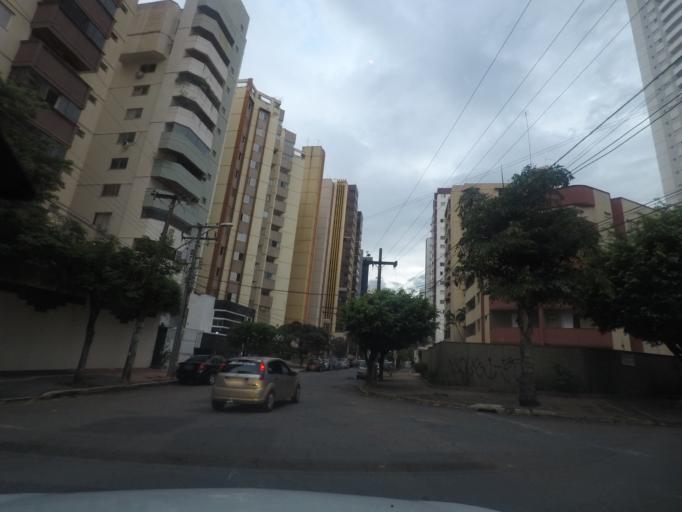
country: BR
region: Goias
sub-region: Goiania
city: Goiania
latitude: -16.7126
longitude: -49.2717
